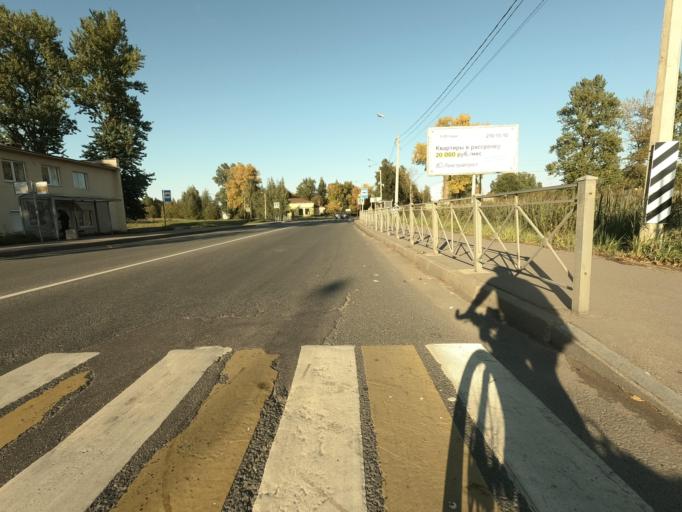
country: RU
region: St.-Petersburg
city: Kolpino
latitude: 59.7567
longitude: 30.6174
